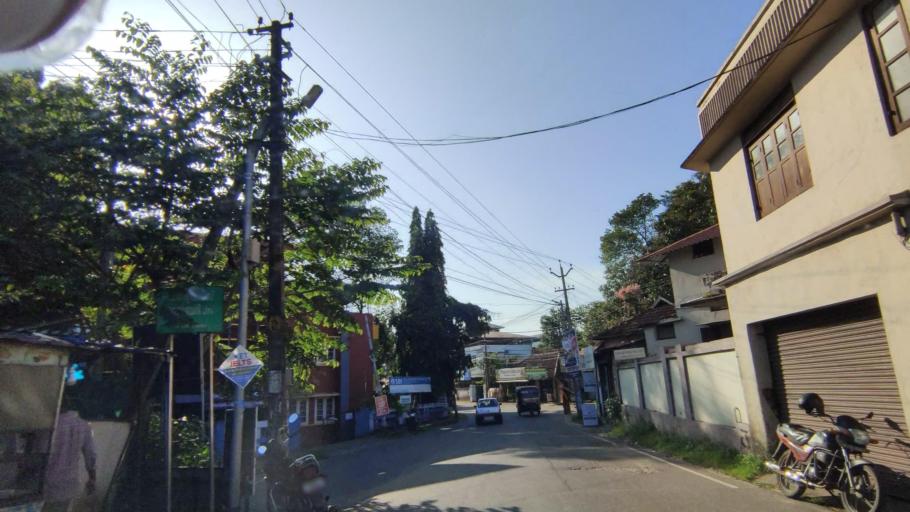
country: IN
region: Kerala
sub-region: Kottayam
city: Kottayam
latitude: 9.5902
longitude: 76.5169
